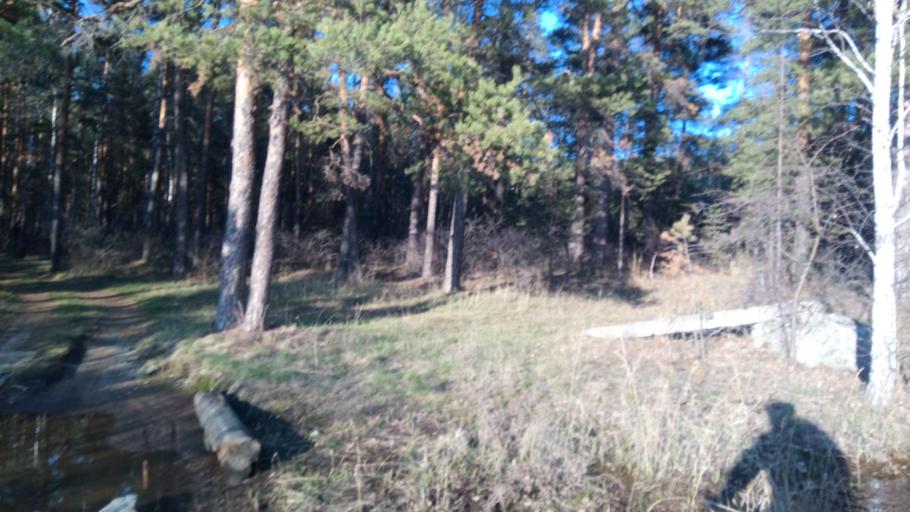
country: RU
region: Chelyabinsk
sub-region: Gorod Chelyabinsk
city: Chelyabinsk
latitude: 55.1339
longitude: 61.3280
